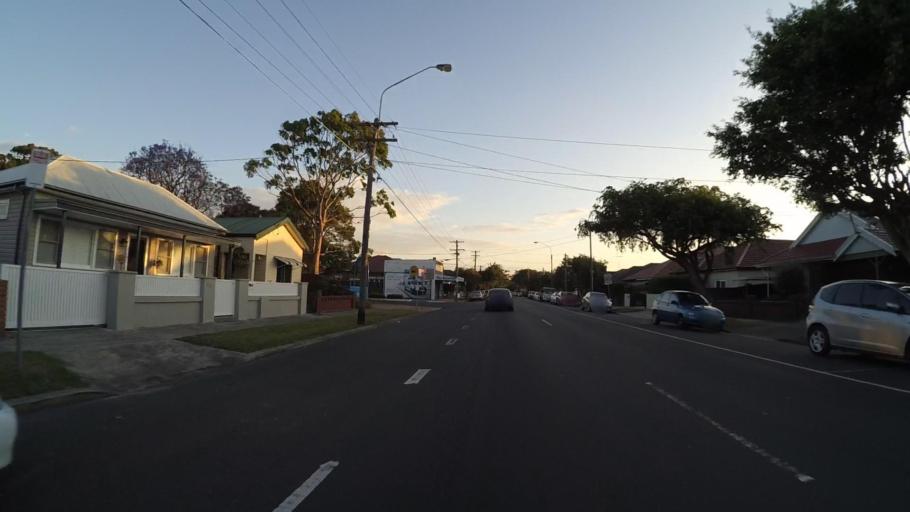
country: AU
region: New South Wales
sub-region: Botany Bay
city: Mascot
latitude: -33.9287
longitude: 151.2058
